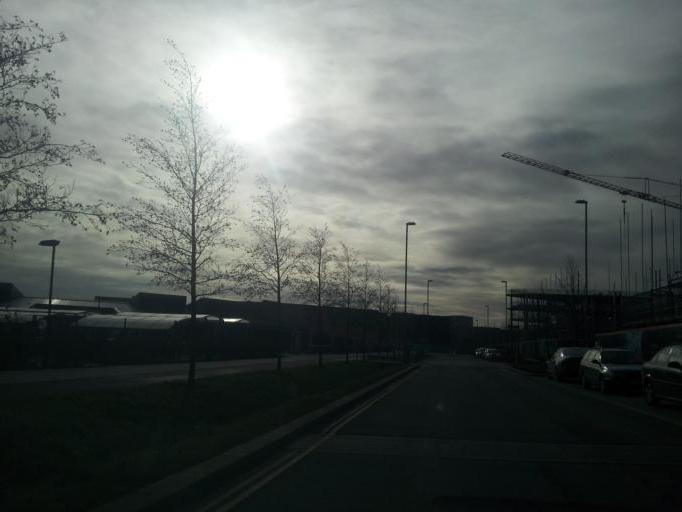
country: GB
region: England
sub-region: Cambridgeshire
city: Girton
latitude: 52.2211
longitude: 0.0893
